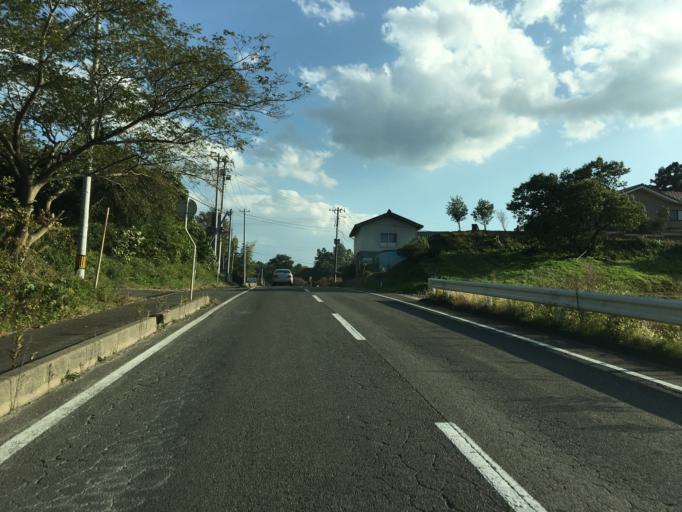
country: JP
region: Fukushima
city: Fukushima-shi
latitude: 37.6798
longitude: 140.5040
